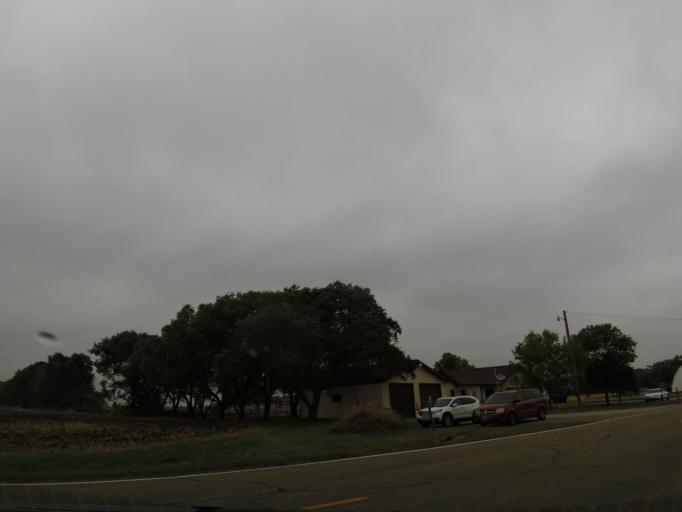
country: US
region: Minnesota
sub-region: Marshall County
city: Warren
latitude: 48.3304
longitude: -96.8271
